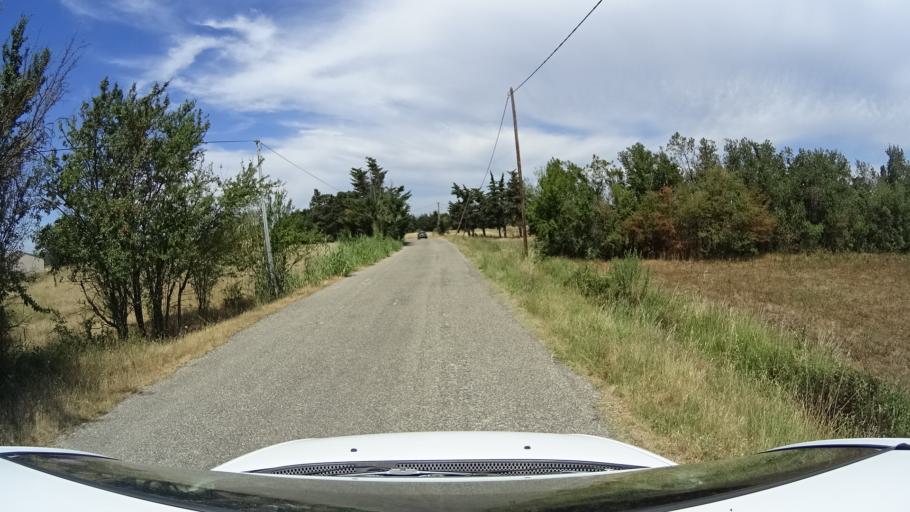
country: FR
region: Provence-Alpes-Cote d'Azur
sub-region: Departement du Vaucluse
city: Cheval-Blanc
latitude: 43.8187
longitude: 5.0590
